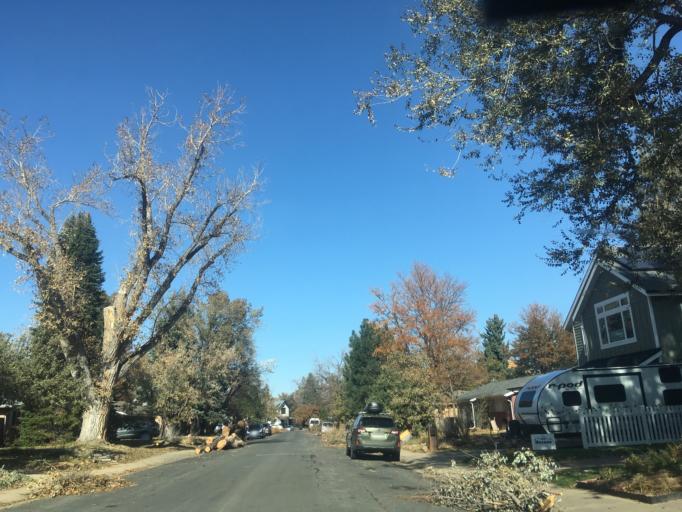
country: US
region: Colorado
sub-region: Boulder County
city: Boulder
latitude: 39.9943
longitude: -105.2540
